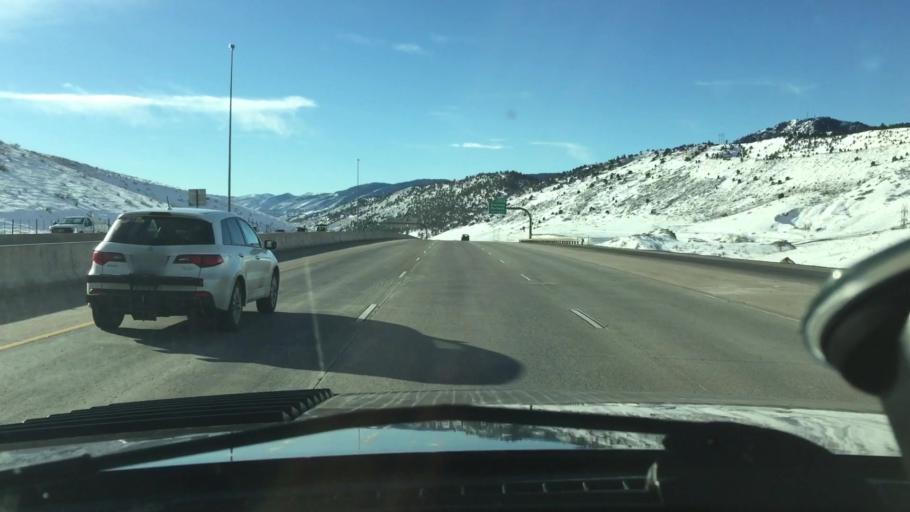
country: US
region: Colorado
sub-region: Jefferson County
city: West Pleasant View
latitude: 39.7078
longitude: -105.1926
